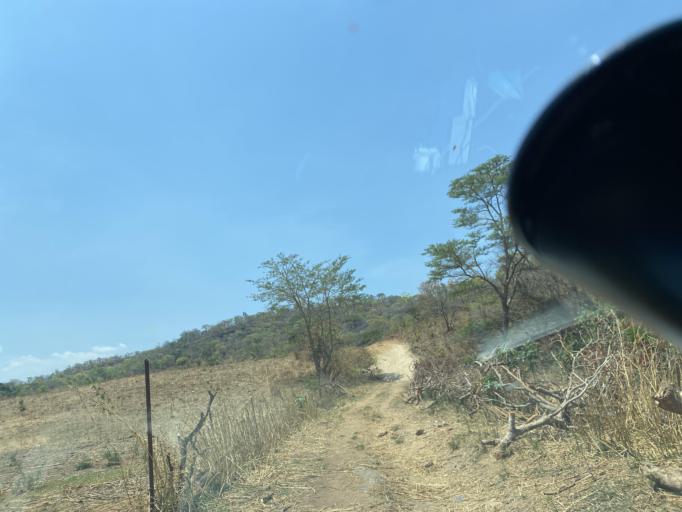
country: ZM
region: Lusaka
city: Kafue
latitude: -15.8074
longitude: 28.4329
